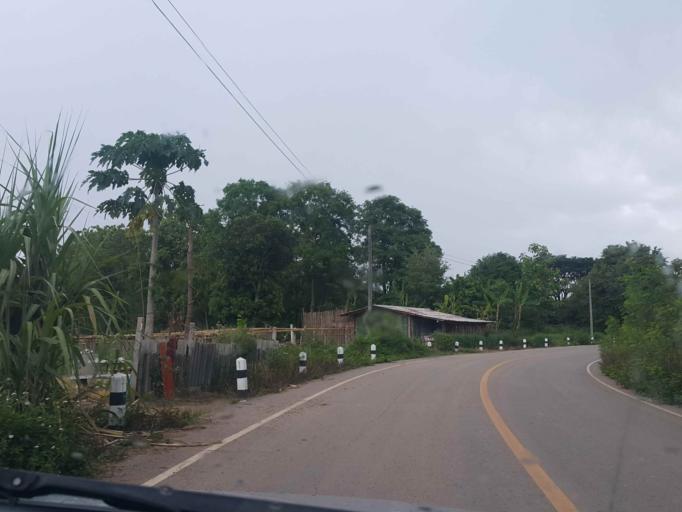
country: TH
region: Phayao
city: Dok Kham Tai
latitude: 19.0359
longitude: 99.9563
